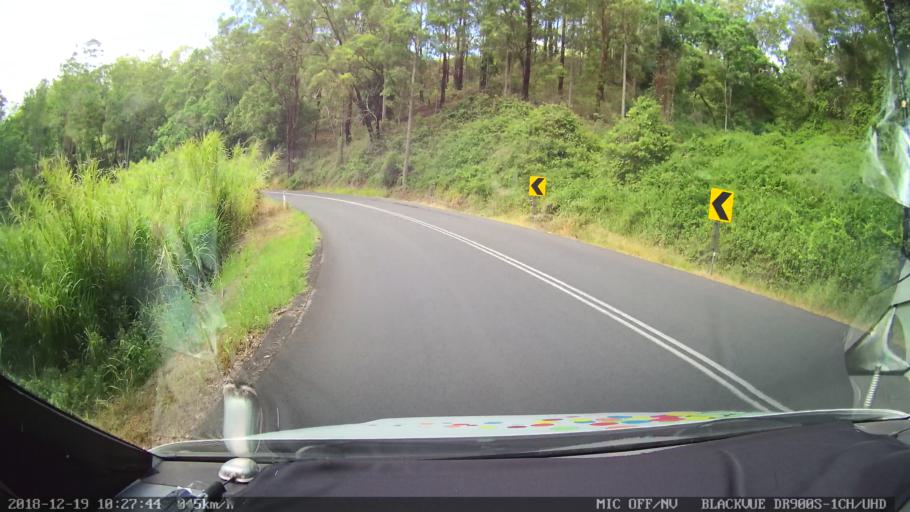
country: AU
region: New South Wales
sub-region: Lismore Municipality
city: Larnook
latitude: -28.5999
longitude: 153.0926
